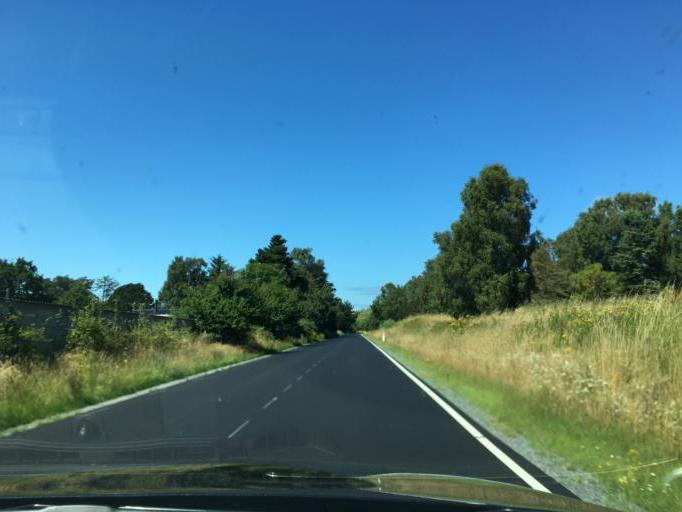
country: DK
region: Capital Region
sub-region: Gribskov Kommune
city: Helsinge
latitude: 56.0870
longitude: 12.1750
